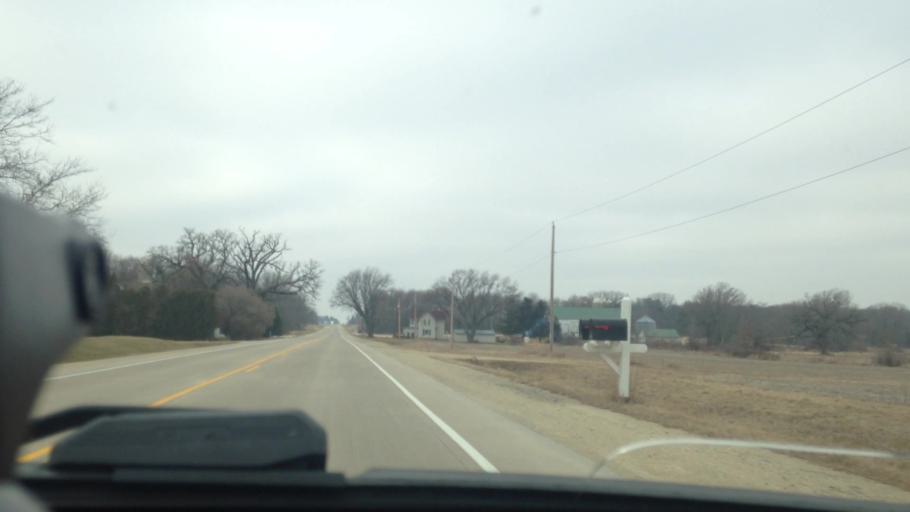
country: US
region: Wisconsin
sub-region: Dodge County
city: Horicon
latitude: 43.4735
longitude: -88.6880
